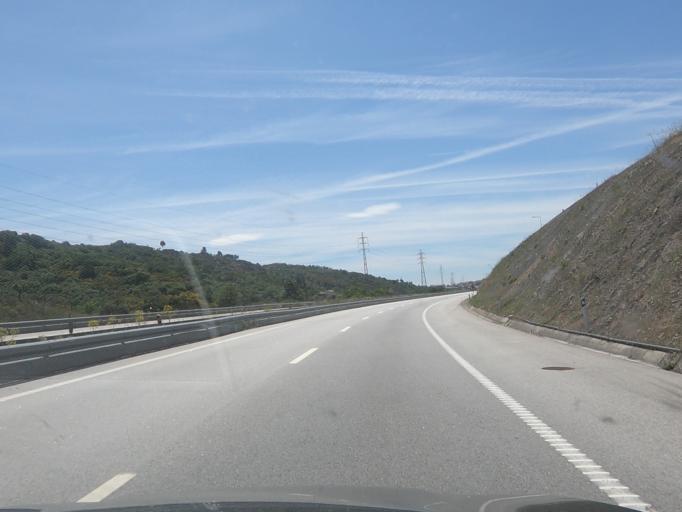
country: PT
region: Guarda
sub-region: Guarda
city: Sequeira
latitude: 40.5861
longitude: -7.2549
